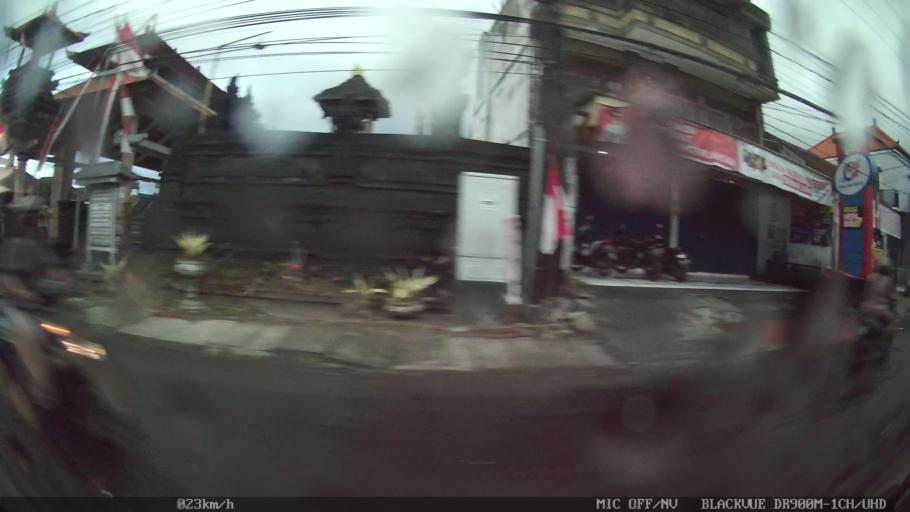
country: ID
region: Bali
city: Banjar Kayangan
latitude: -8.6251
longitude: 115.2238
